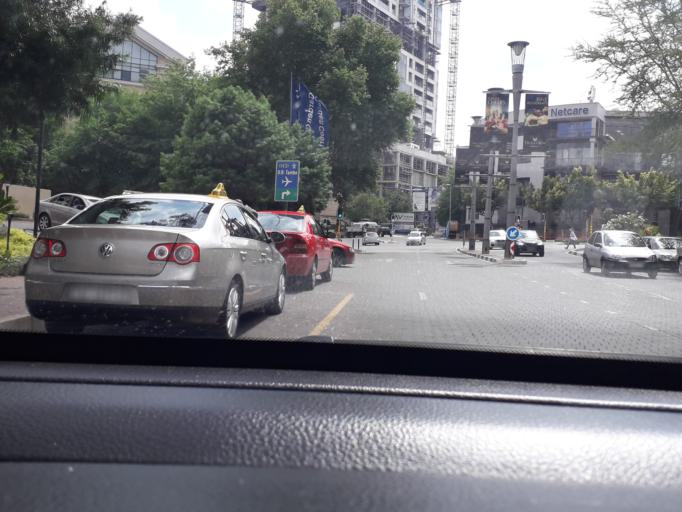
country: ZA
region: Gauteng
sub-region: City of Johannesburg Metropolitan Municipality
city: Johannesburg
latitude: -26.1058
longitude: 28.0544
